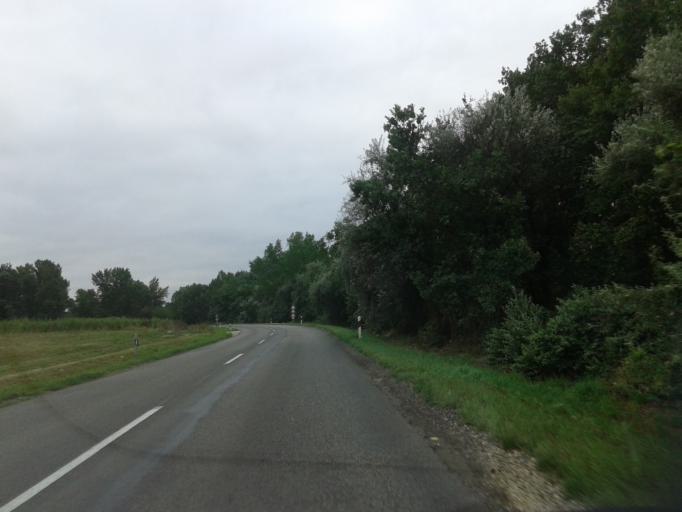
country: HU
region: Pest
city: Domsod
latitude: 47.1314
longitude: 18.9954
